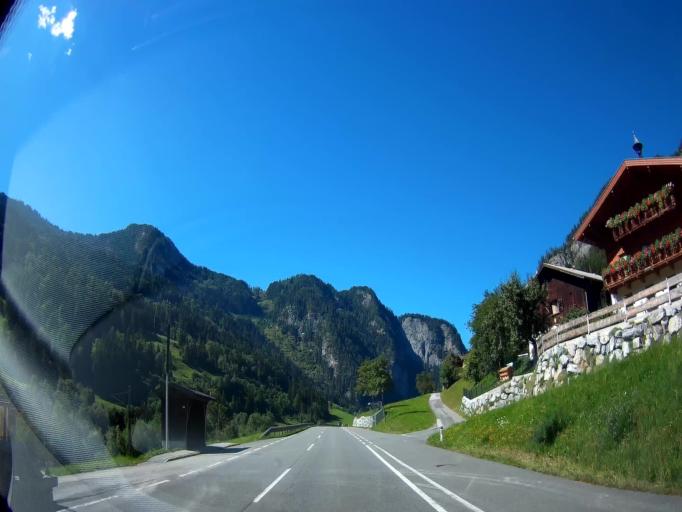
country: AT
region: Salzburg
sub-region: Politischer Bezirk Sankt Johann im Pongau
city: Dorfgastein
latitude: 47.2644
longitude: 13.0828
